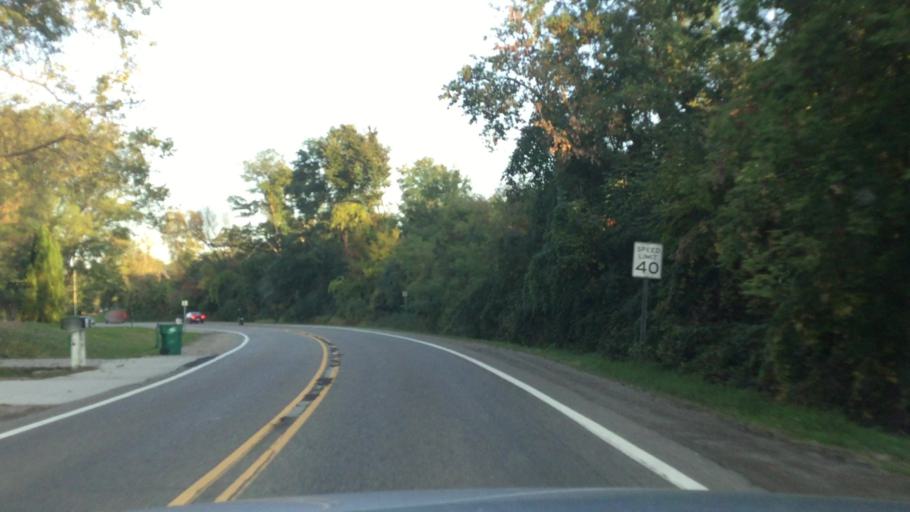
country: US
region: Michigan
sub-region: Oakland County
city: Keego Harbor
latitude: 42.6234
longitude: -83.3742
